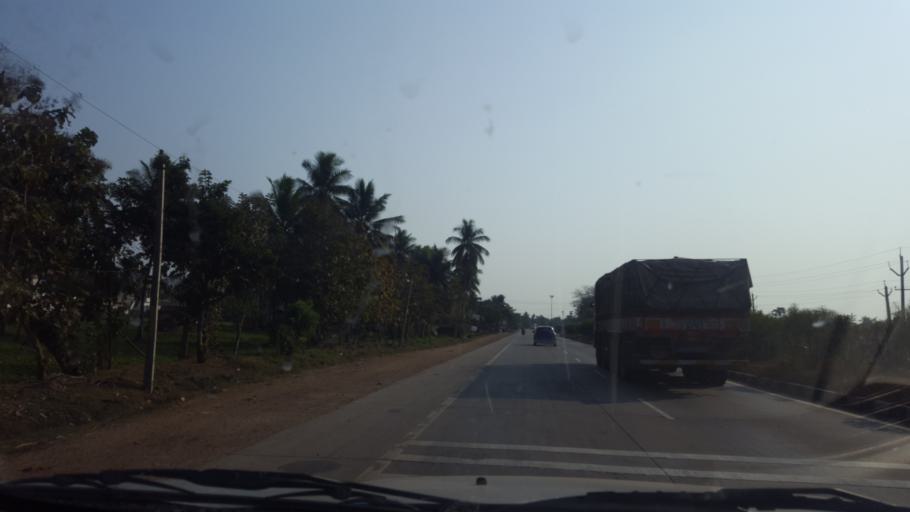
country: IN
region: Andhra Pradesh
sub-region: Vishakhapatnam
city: Etikoppaka
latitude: 17.4870
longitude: 82.7870
